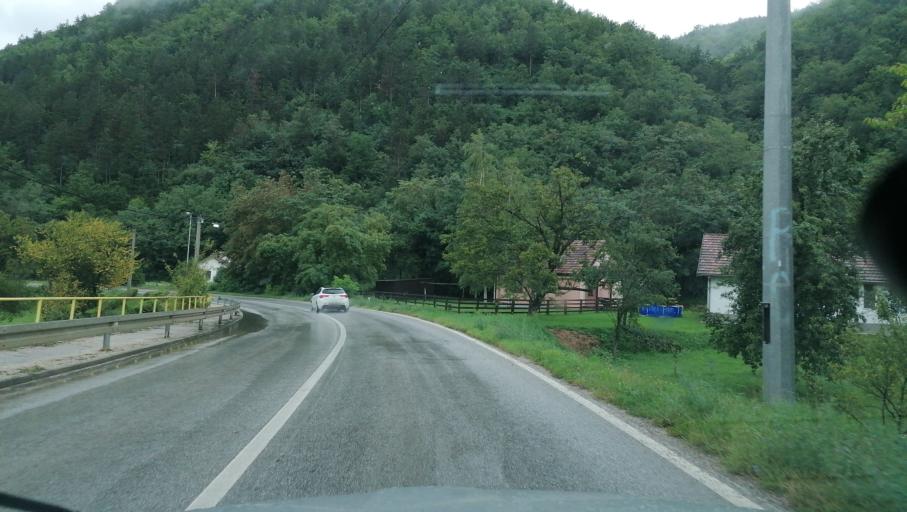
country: BA
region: Federation of Bosnia and Herzegovina
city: Gorazde
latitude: 43.6802
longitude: 19.0140
